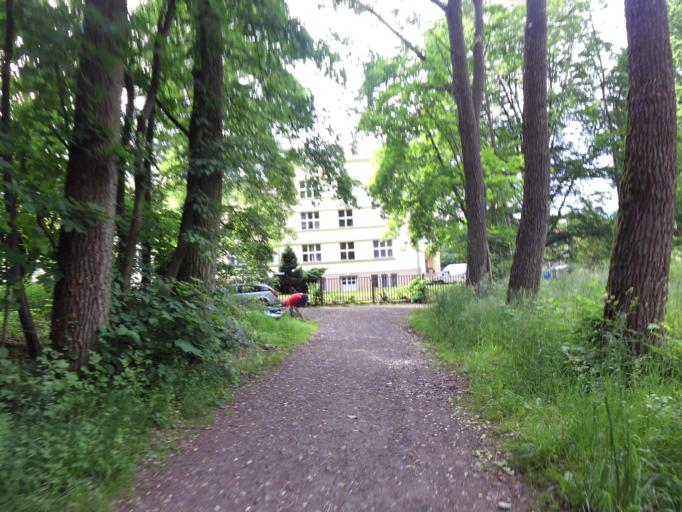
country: CZ
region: Ustecky
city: Varnsdorf
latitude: 50.8933
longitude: 14.6127
